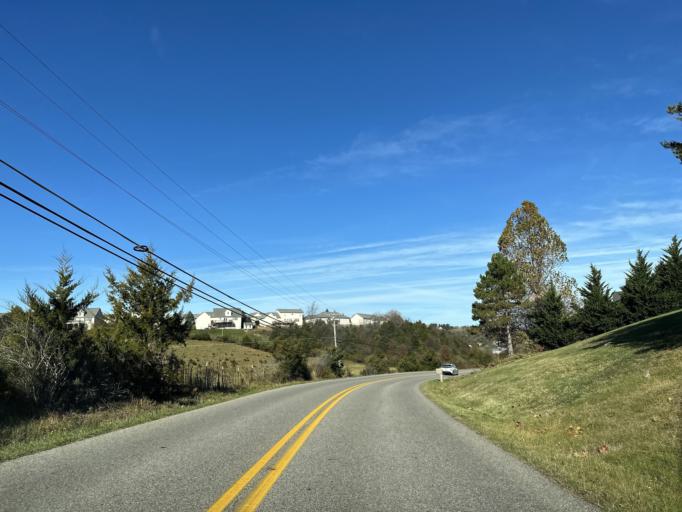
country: US
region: Virginia
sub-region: Augusta County
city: Fishersville
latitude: 38.1051
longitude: -78.9630
